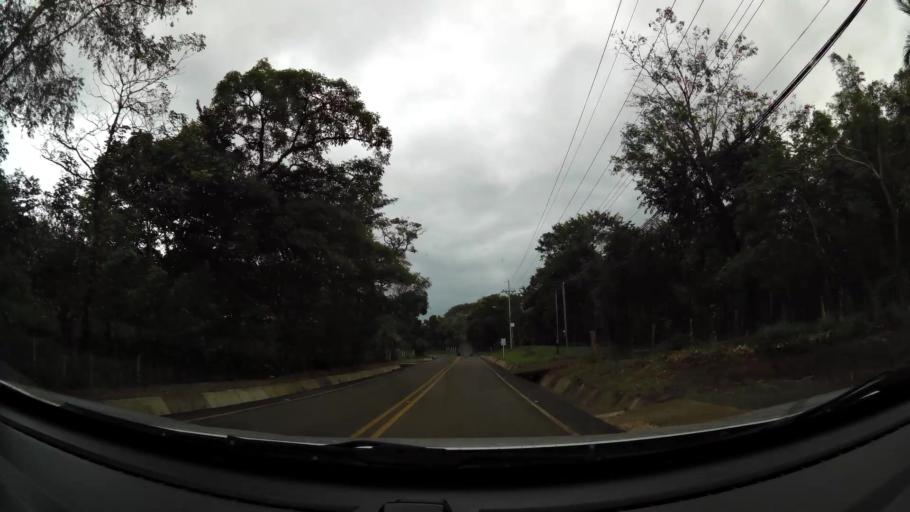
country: CR
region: Puntarenas
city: Esparza
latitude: 9.9596
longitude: -84.5964
